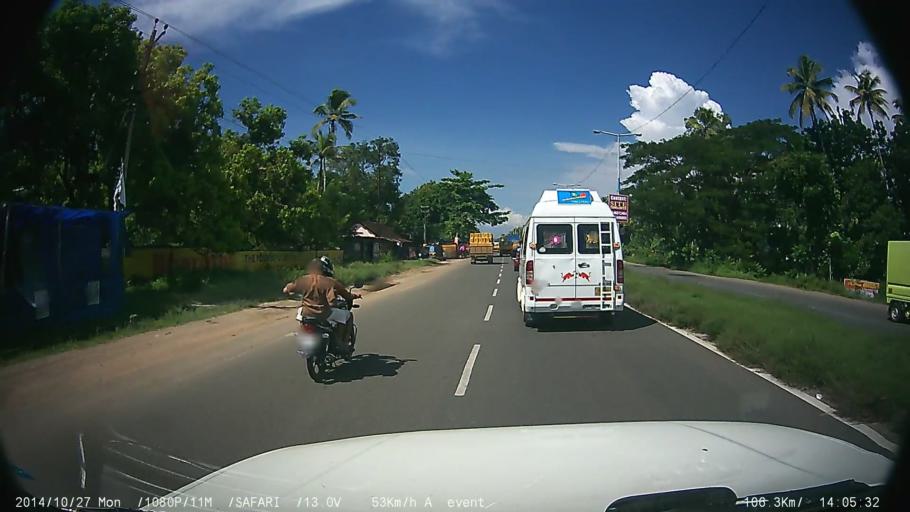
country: IN
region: Kerala
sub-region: Alappuzha
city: Vayalar
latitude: 9.7419
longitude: 76.3186
